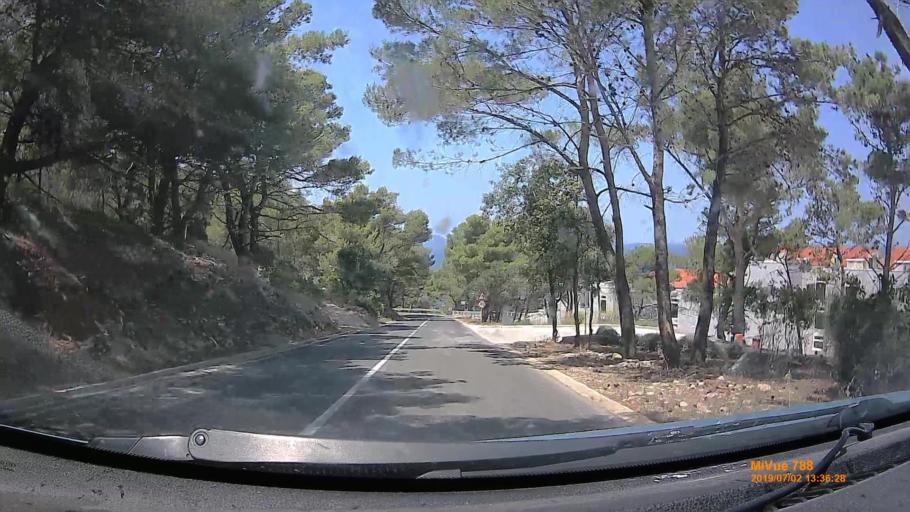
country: HR
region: Primorsko-Goranska
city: Mali Losinj
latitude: 44.5234
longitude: 14.4956
